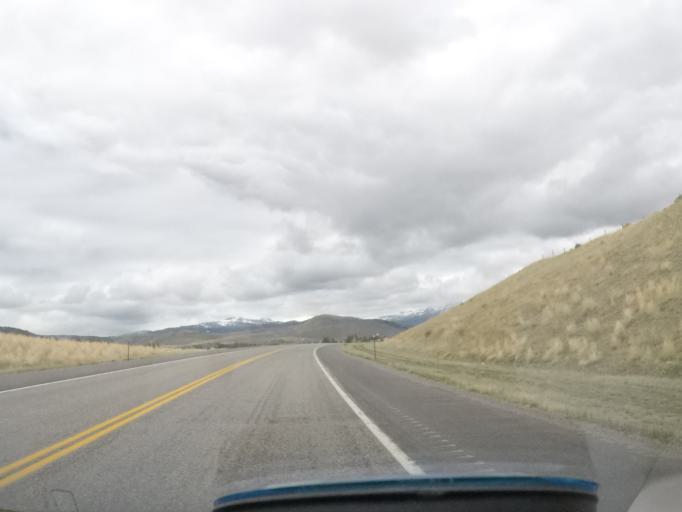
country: US
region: Wyoming
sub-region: Sublette County
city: Pinedale
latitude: 43.5869
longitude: -109.7711
